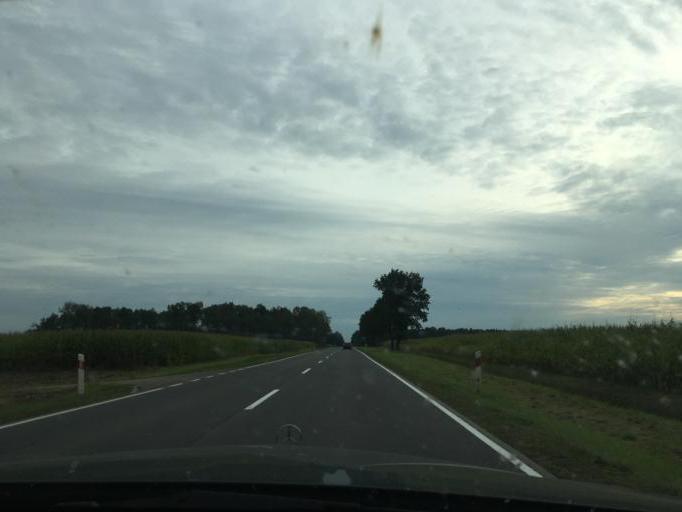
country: PL
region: Masovian Voivodeship
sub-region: Powiat ostrowski
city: Ostrow Mazowiecka
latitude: 52.9064
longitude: 21.8727
